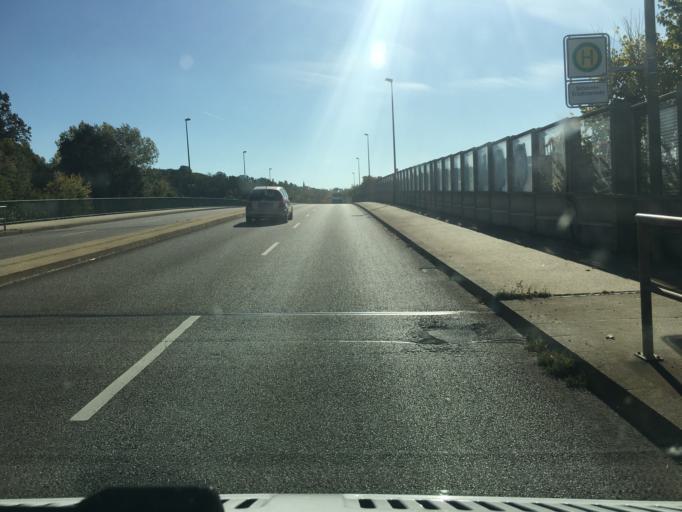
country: DE
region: Saxony
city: Zwickau
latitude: 50.7247
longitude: 12.5002
